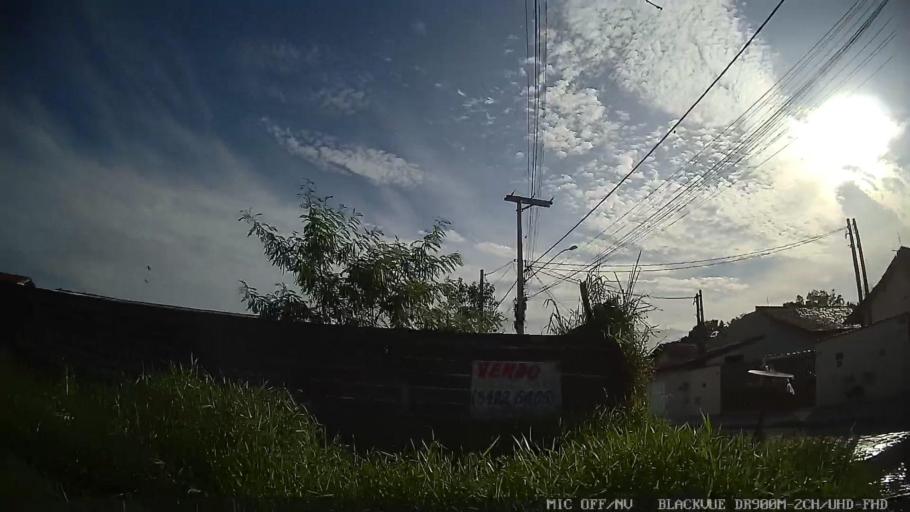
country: BR
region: Sao Paulo
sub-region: Itanhaem
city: Itanhaem
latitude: -24.1603
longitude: -46.7597
